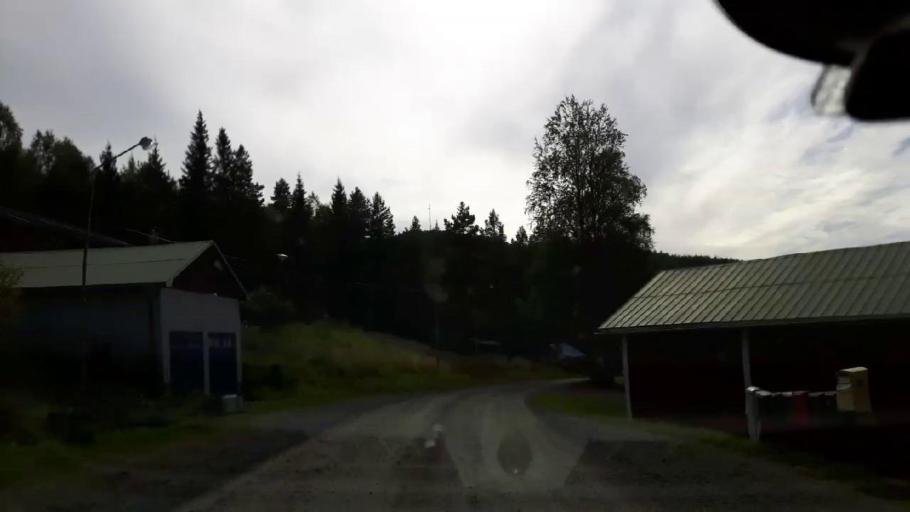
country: SE
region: Jaemtland
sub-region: Ragunda Kommun
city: Hammarstrand
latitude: 63.1421
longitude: 16.2026
